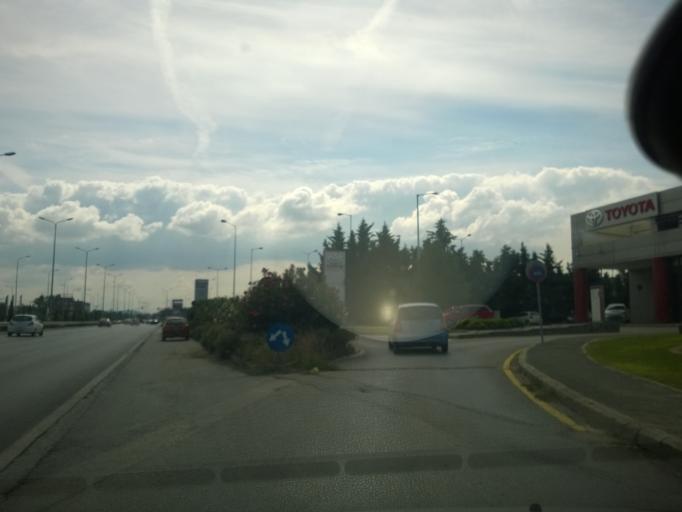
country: GR
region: Central Macedonia
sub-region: Nomos Thessalonikis
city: Thermi
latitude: 40.5497
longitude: 22.9824
